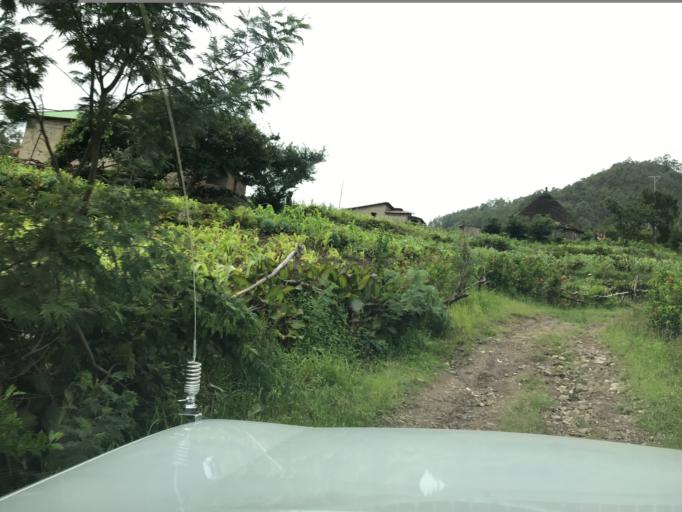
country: TL
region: Ainaro
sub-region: Ainaro
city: Ainaro
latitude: -8.8691
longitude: 125.5522
